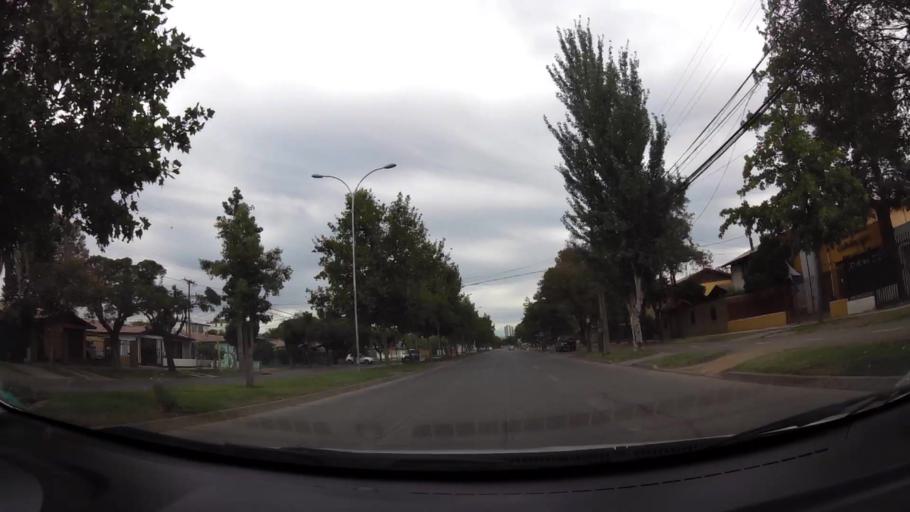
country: CL
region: O'Higgins
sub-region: Provincia de Cachapoal
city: Rancagua
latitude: -34.1592
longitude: -70.7328
